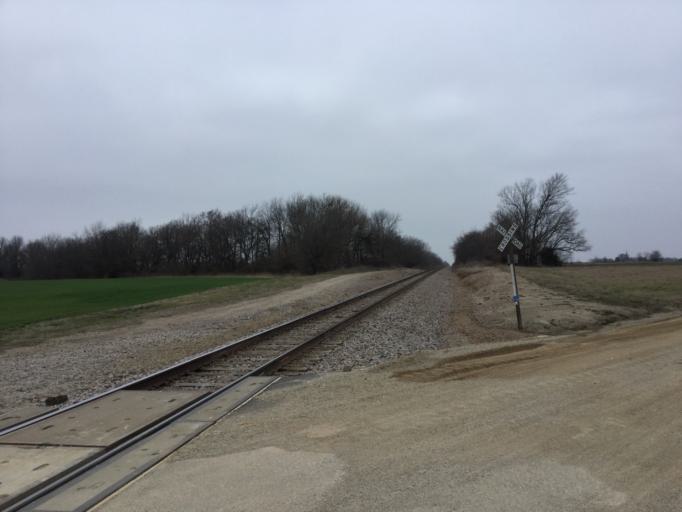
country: US
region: Kansas
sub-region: Cherokee County
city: Baxter Springs
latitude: 37.0523
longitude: -94.7587
